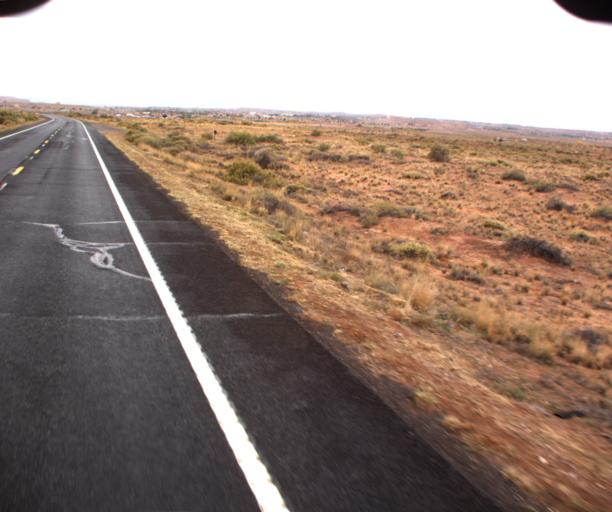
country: US
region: Arizona
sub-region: Coconino County
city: Tuba City
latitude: 36.1309
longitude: -111.1882
